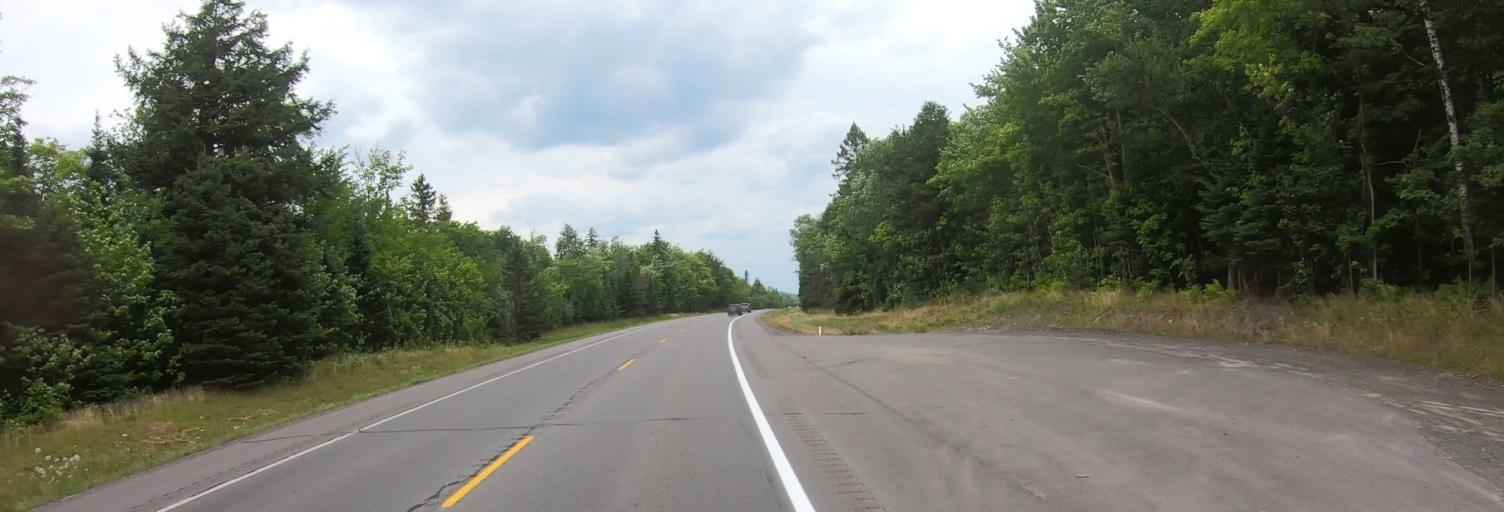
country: US
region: Michigan
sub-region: Baraga County
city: L'Anse
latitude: 46.5900
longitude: -88.4749
